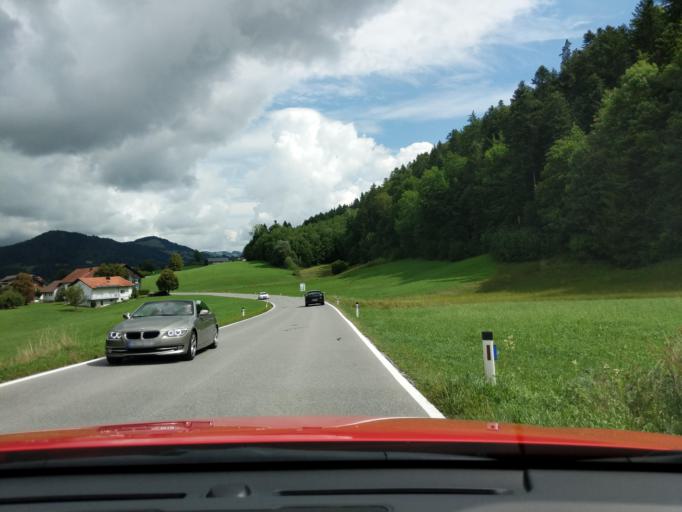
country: AT
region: Vorarlberg
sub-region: Politischer Bezirk Bregenz
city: Riefensberg
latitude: 47.5143
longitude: 9.9595
